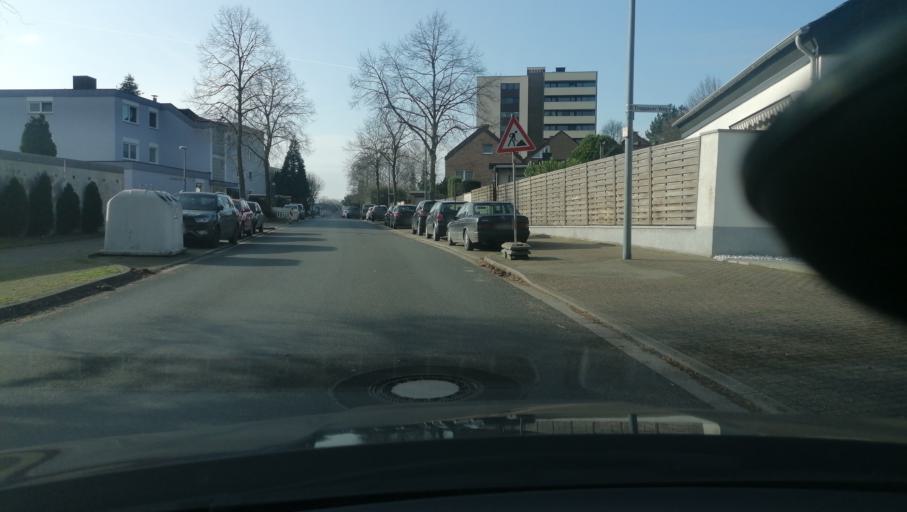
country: DE
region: North Rhine-Westphalia
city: Herten
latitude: 51.6098
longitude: 7.1513
